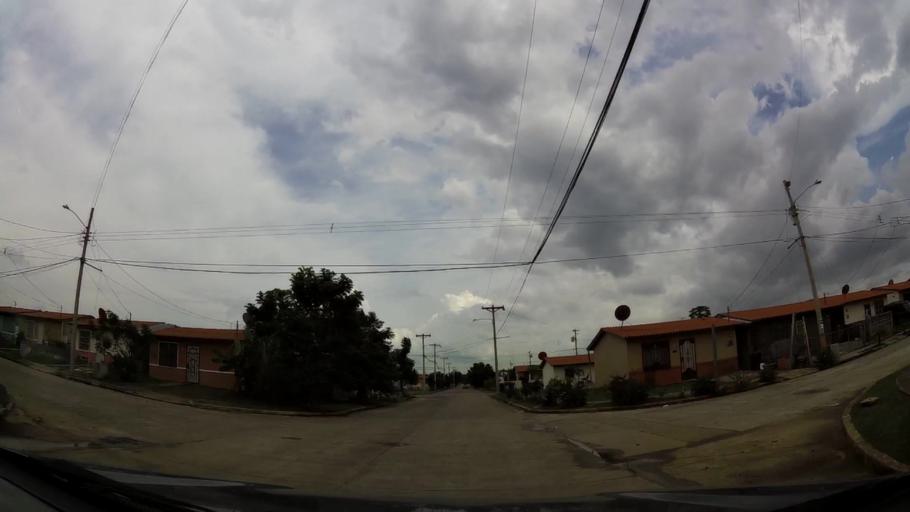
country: PA
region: Panama
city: Cabra Numero Uno
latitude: 9.1160
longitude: -79.3247
